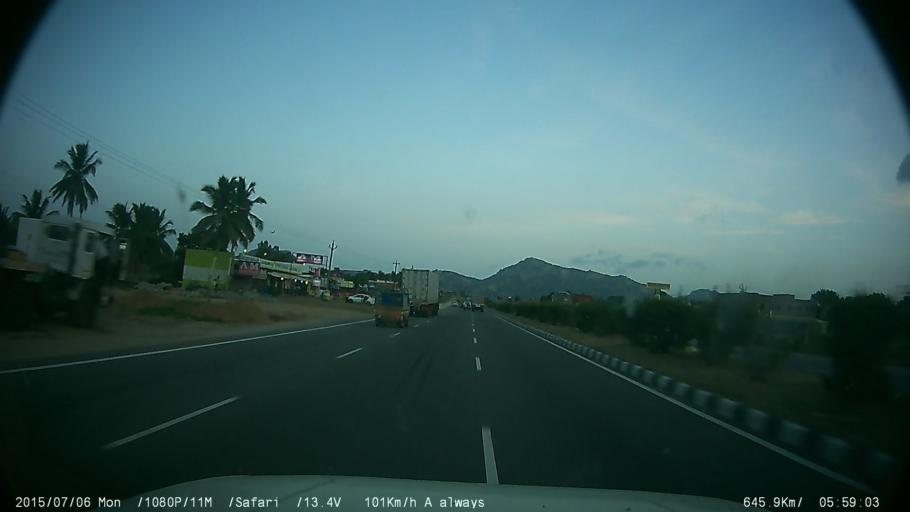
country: IN
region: Tamil Nadu
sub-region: Krishnagiri
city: Krishnagiri
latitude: 12.5902
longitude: 78.1424
